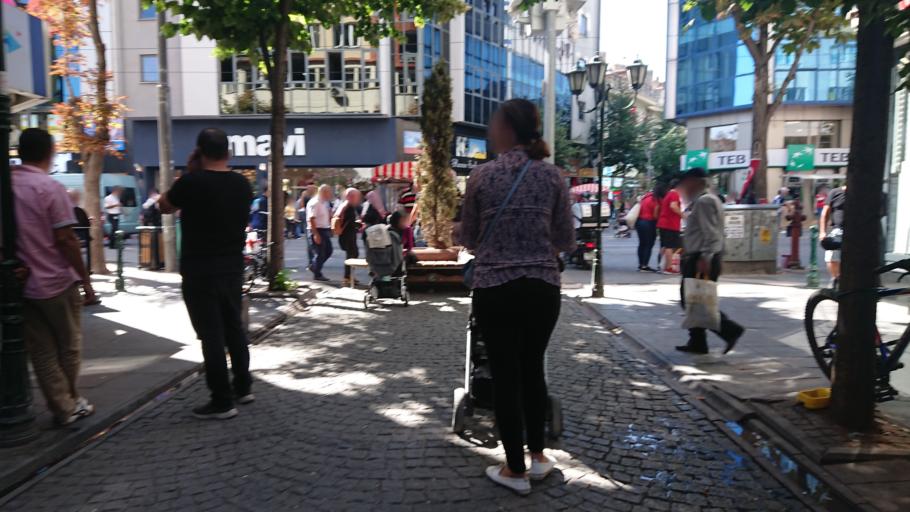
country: TR
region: Eskisehir
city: Eskisehir
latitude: 39.7751
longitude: 30.5181
